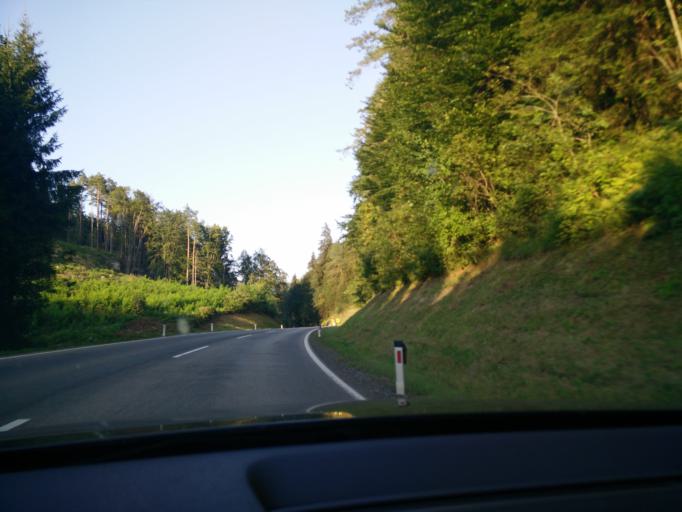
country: AT
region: Carinthia
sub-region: Politischer Bezirk Klagenfurt Land
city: Maria Rain
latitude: 46.5534
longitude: 14.2742
